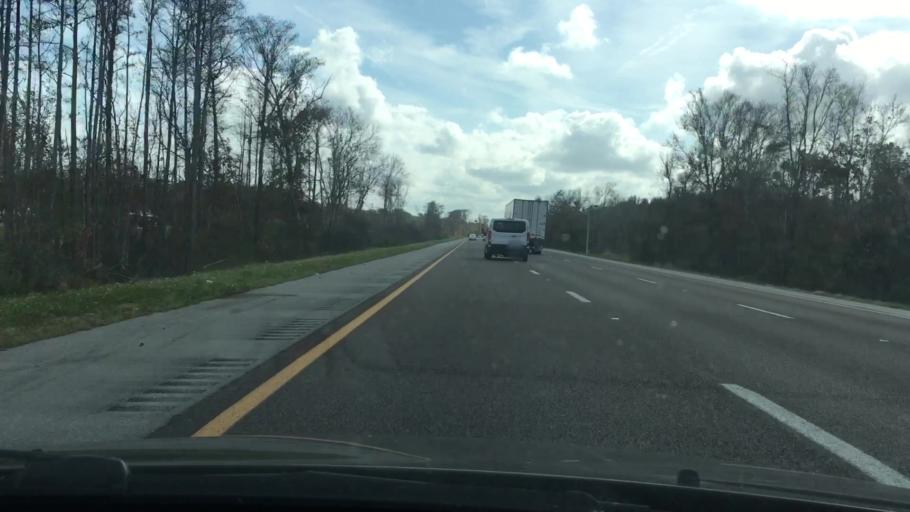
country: US
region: Florida
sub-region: Volusia County
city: Oak Hill
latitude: 28.8765
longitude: -80.9219
